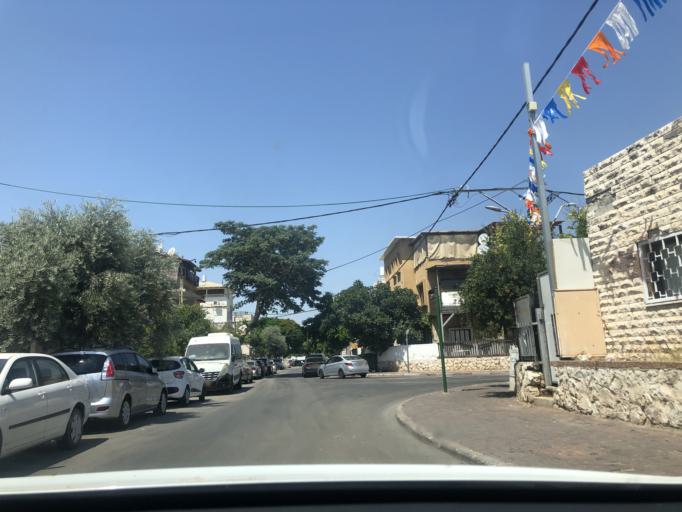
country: IL
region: Central District
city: Lod
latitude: 31.9580
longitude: 34.9024
